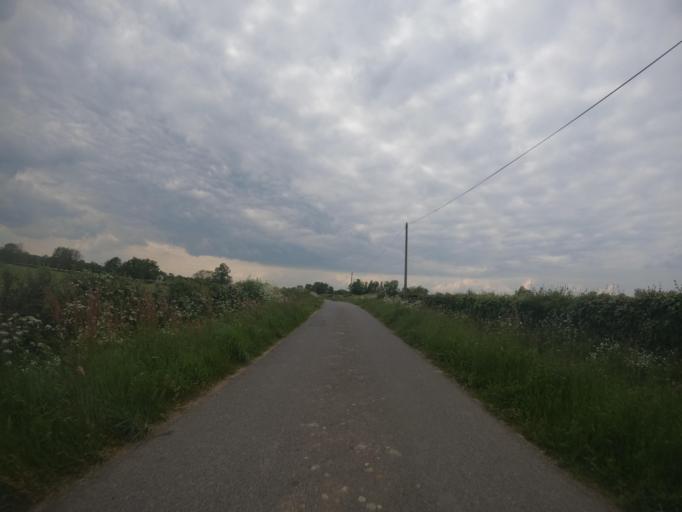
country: FR
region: Poitou-Charentes
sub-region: Departement des Deux-Sevres
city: Chiche
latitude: 46.8555
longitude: -0.3221
